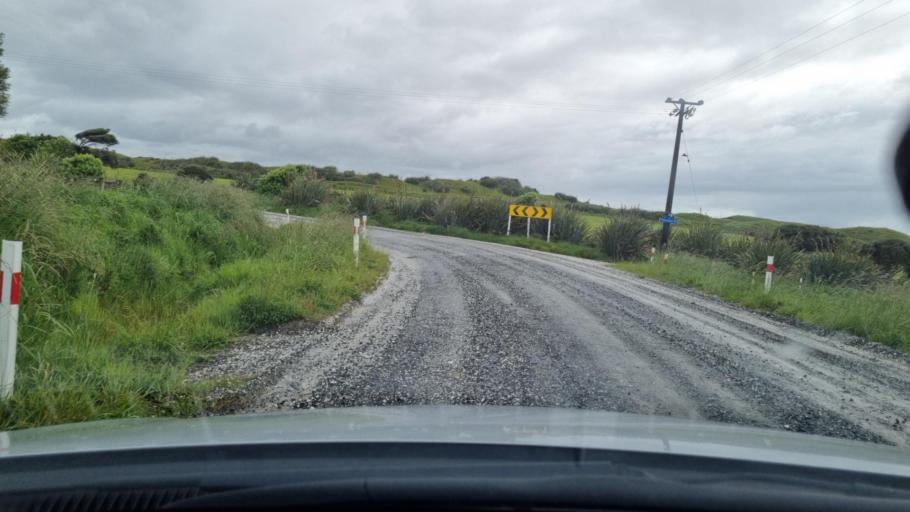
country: NZ
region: Southland
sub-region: Invercargill City
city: Bluff
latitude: -46.5205
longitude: 168.2725
